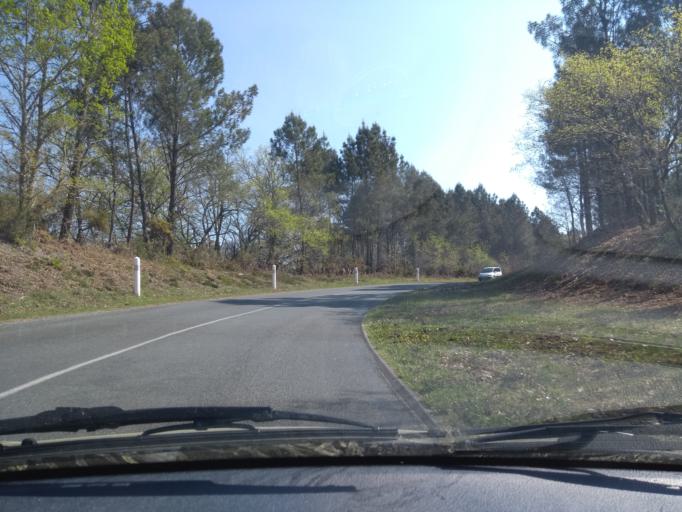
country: FR
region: Aquitaine
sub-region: Departement de la Gironde
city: Belin-Beliet
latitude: 44.5200
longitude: -0.7504
